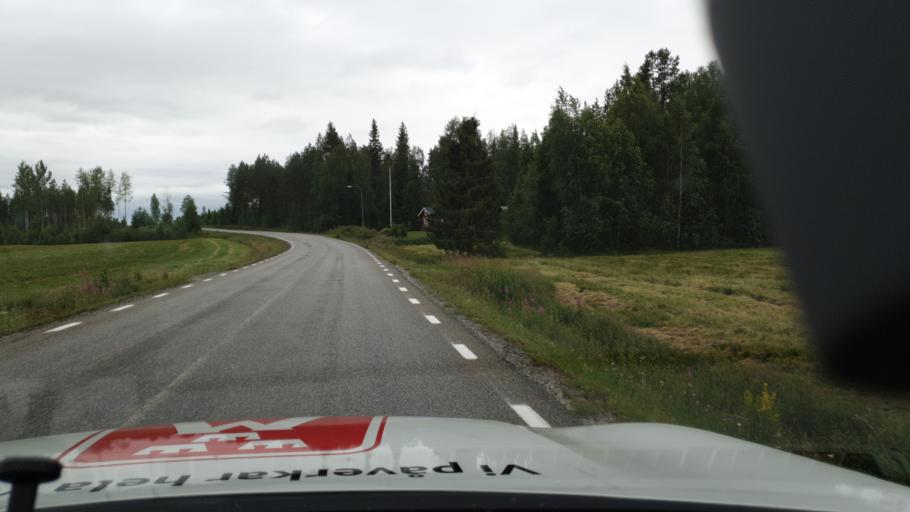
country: SE
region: Vaesterbotten
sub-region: Umea Kommun
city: Saevar
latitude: 64.0860
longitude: 20.5011
